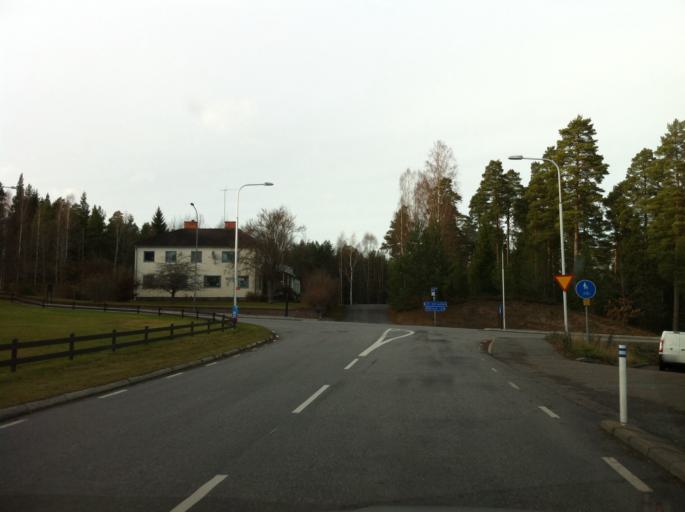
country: SE
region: Kalmar
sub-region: Hultsfreds Kommun
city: Virserum
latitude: 57.4087
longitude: 15.6186
